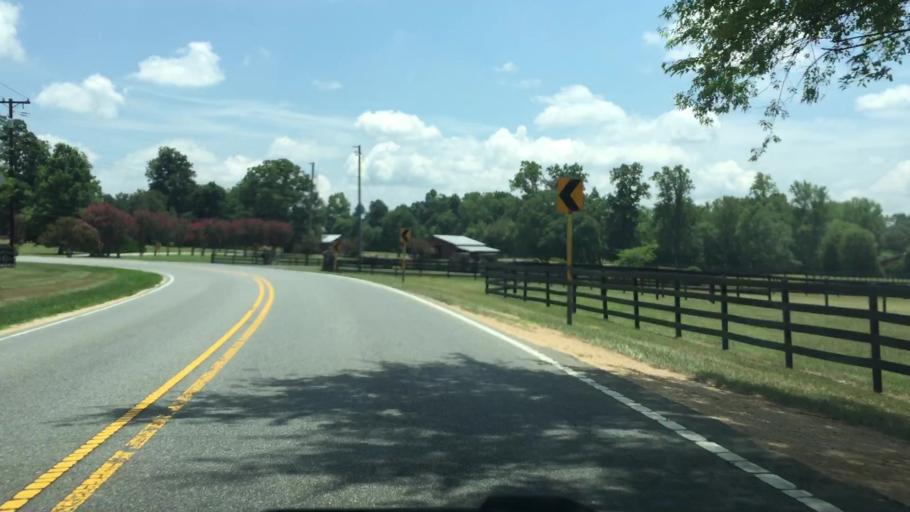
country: US
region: North Carolina
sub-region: Rowan County
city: Enochville
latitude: 35.4310
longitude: -80.7236
